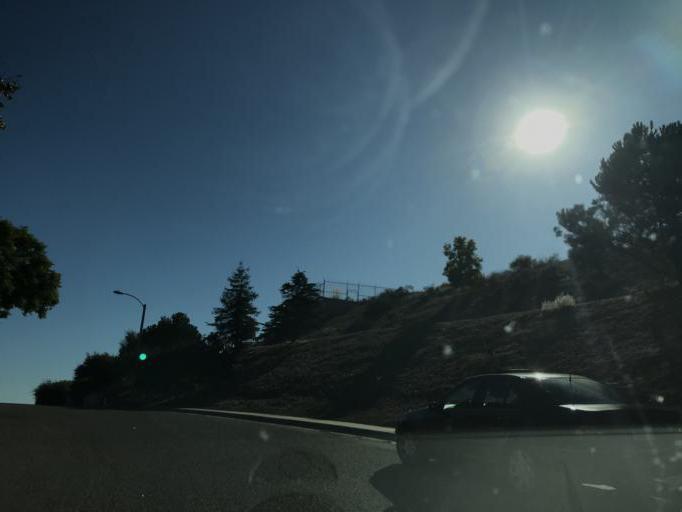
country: US
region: California
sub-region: Santa Barbara County
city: Goleta
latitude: 34.4485
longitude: -119.7813
